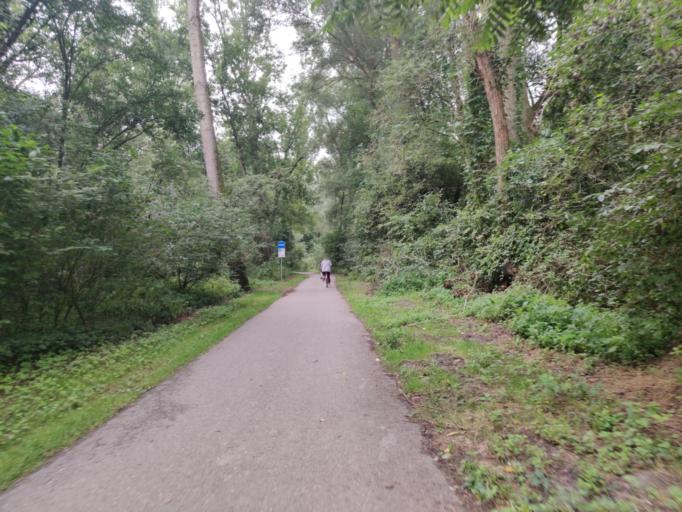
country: AT
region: Lower Austria
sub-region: Politischer Bezirk Tulln
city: Kirchberg am Wagram
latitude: 48.3603
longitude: 15.8797
